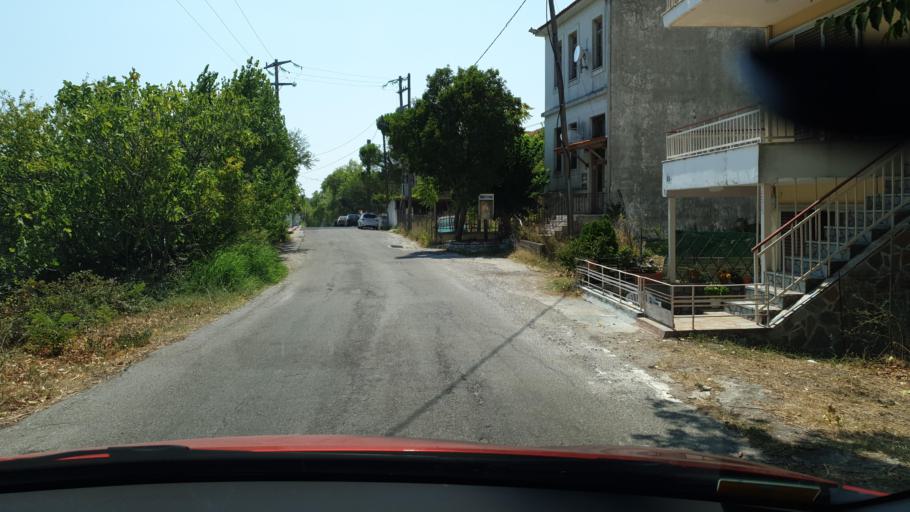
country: GR
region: Central Greece
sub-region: Nomos Evvoias
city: Oxilithos
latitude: 38.5761
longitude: 24.0615
